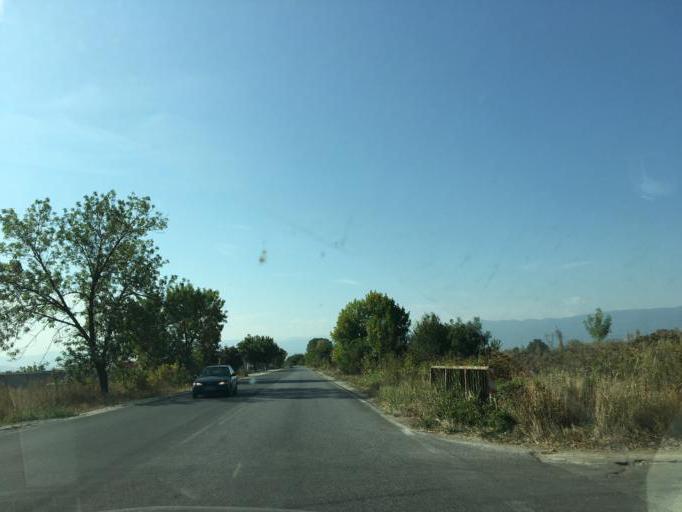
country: BG
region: Pazardzhik
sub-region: Obshtina Pazardzhik
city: Pazardzhik
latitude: 42.2278
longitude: 24.3105
